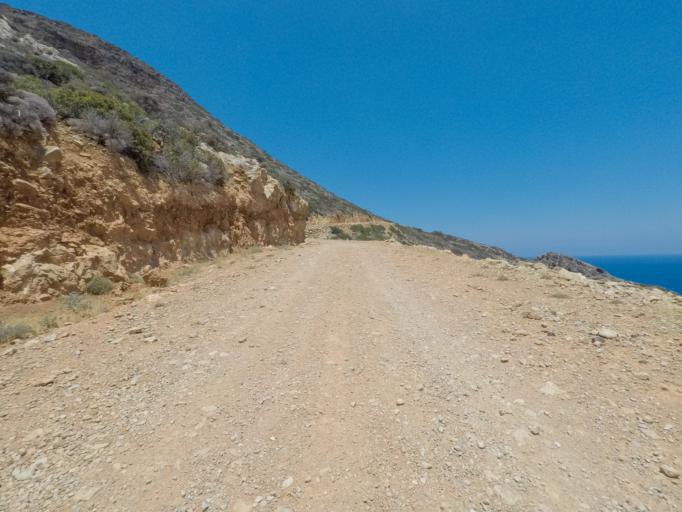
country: GR
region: Crete
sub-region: Nomos Lasithiou
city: Elounda
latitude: 35.3174
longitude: 25.7538
